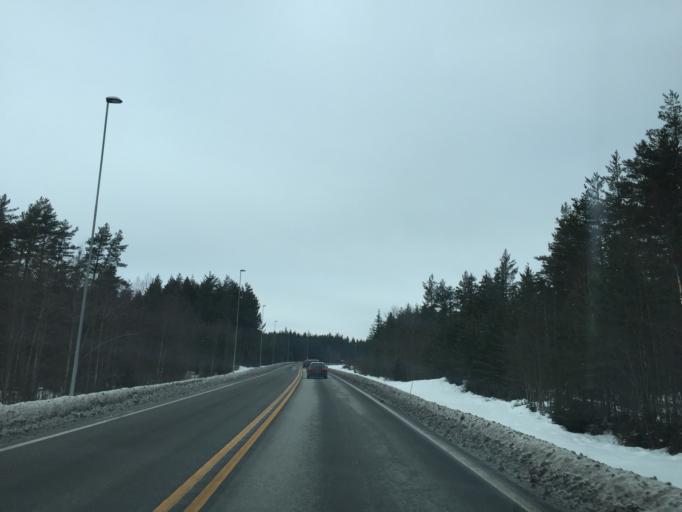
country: NO
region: Hedmark
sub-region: Loten
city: Loten
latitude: 60.7735
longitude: 11.3079
